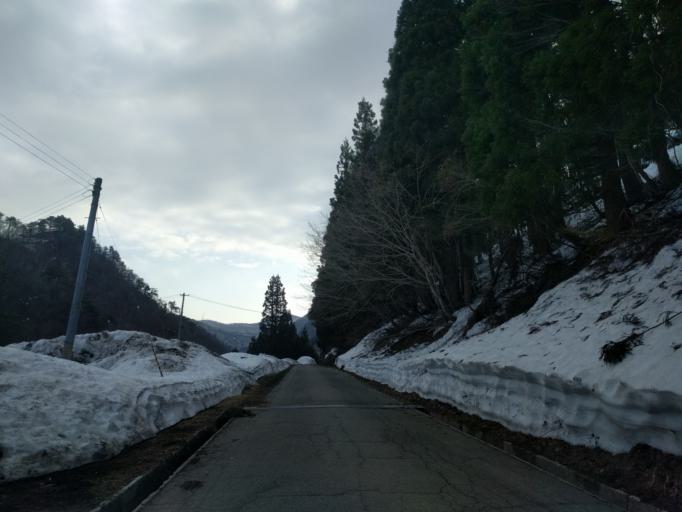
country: JP
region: Fukushima
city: Kitakata
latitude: 37.7300
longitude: 139.9461
